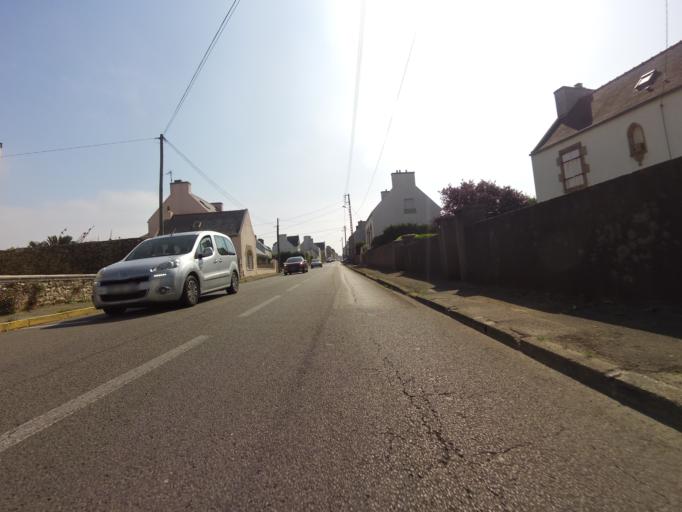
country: FR
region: Brittany
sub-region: Departement du Finistere
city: Plouhinec
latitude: 48.0153
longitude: -4.4939
